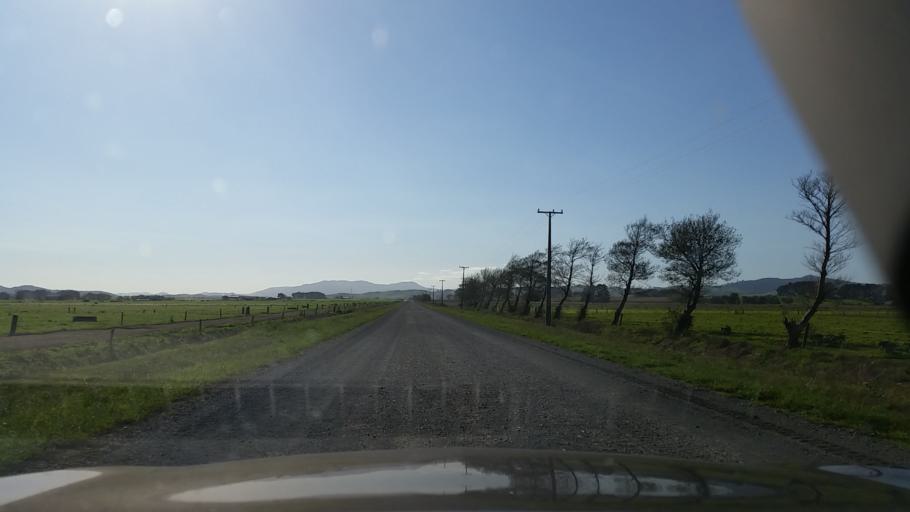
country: NZ
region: Waikato
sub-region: Hamilton City
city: Hamilton
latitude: -37.6433
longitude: 175.4321
